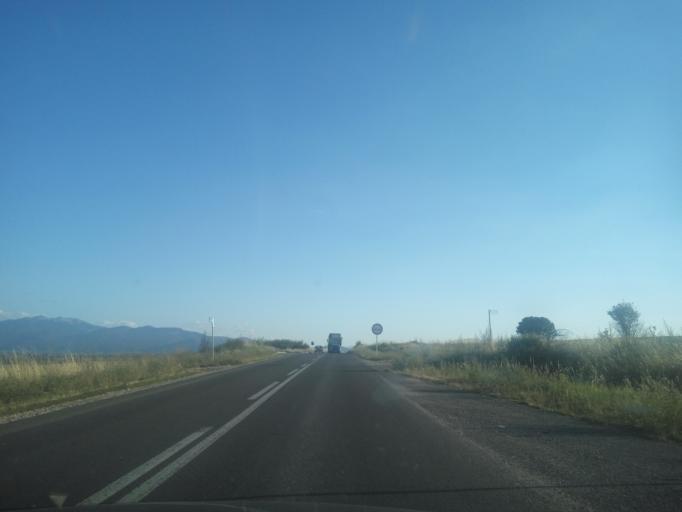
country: XK
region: Gjakova
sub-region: Komuna e Gjakoves
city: Gjakove
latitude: 42.4445
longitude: 20.4917
